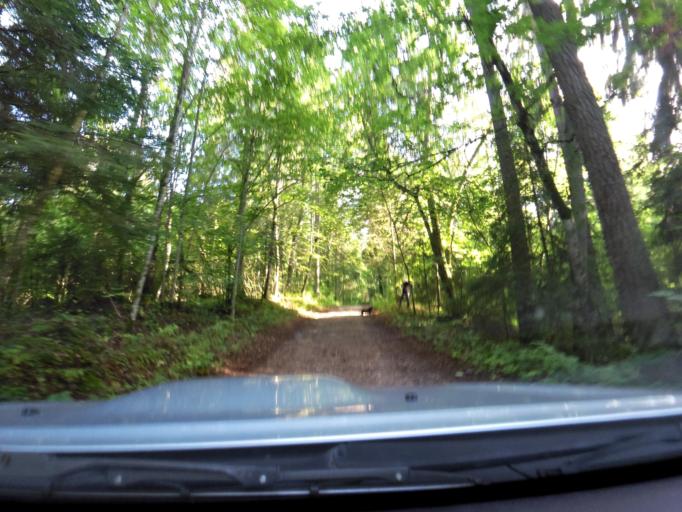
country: LT
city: Trakai
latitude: 54.6461
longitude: 24.9761
